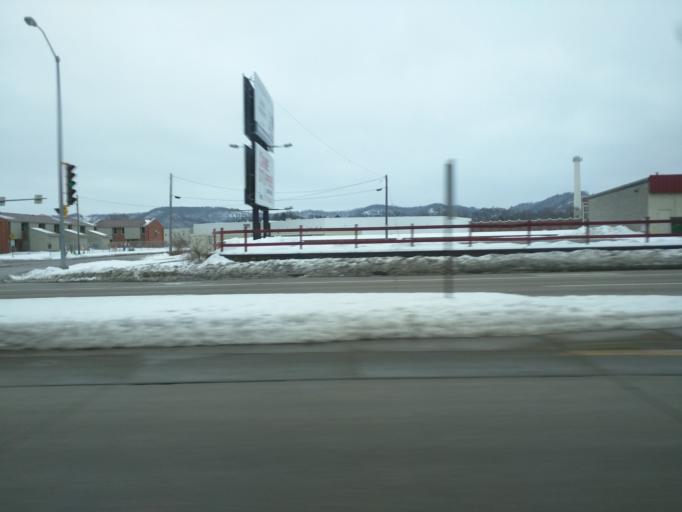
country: US
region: Wisconsin
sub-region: La Crosse County
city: North La Crosse
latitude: 43.8356
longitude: -91.2396
